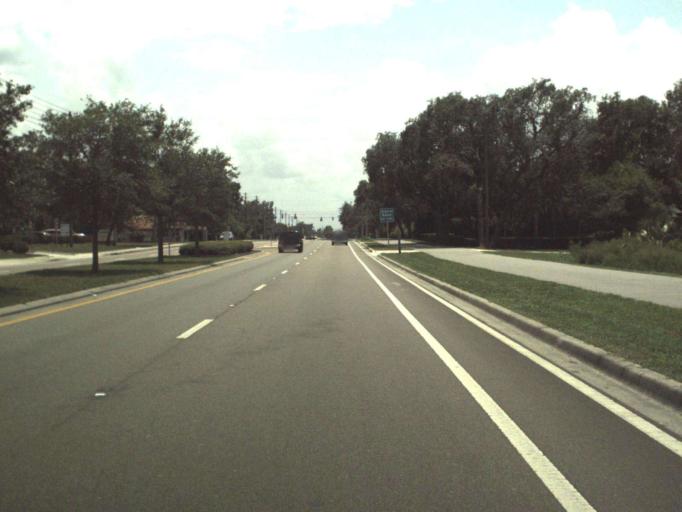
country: US
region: Florida
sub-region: Seminole County
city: Oviedo
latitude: 28.6507
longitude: -81.2292
